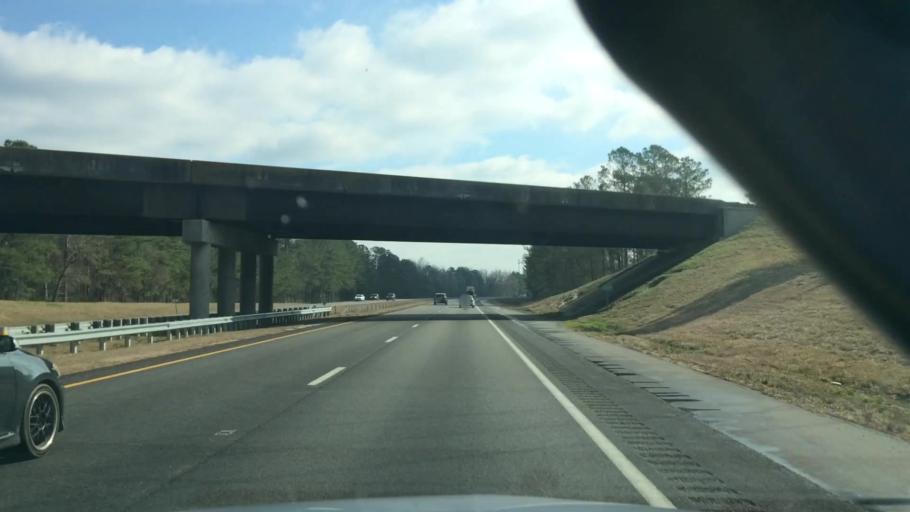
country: US
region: North Carolina
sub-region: Pender County
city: Burgaw
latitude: 34.6121
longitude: -77.9208
